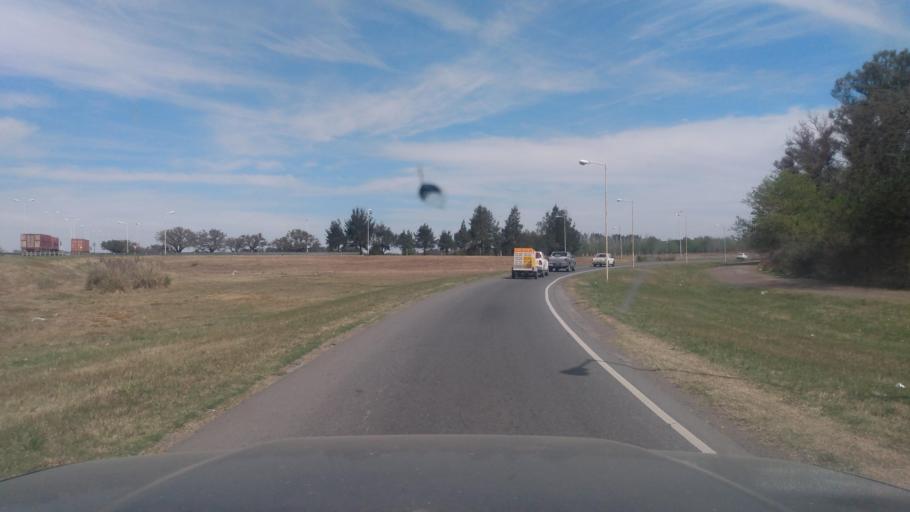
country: AR
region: Buenos Aires
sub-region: Partido de Lujan
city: Lujan
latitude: -34.5713
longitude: -59.0376
